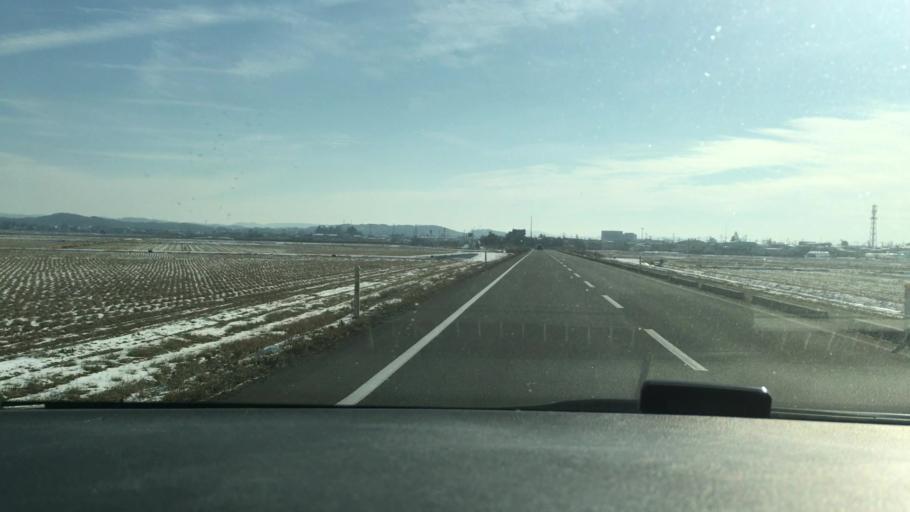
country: JP
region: Iwate
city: Ichinoseki
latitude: 38.7801
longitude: 141.1264
